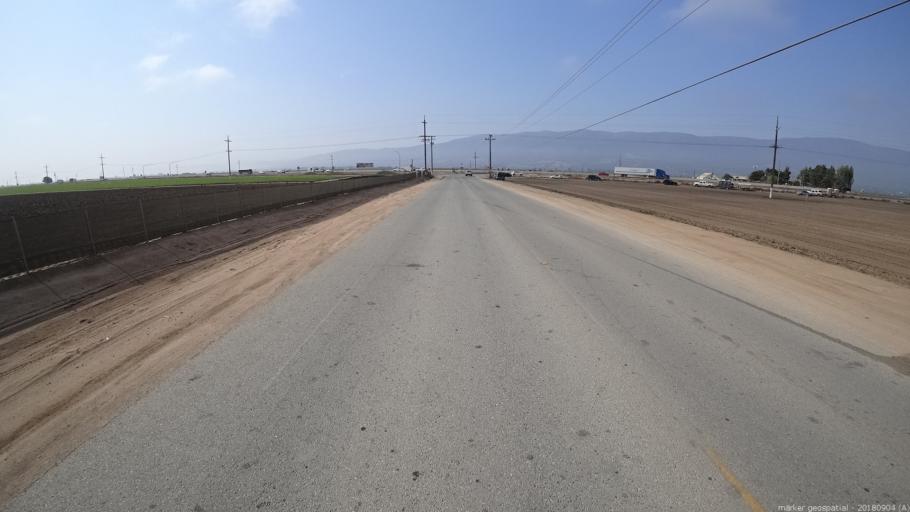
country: US
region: California
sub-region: Monterey County
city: Soledad
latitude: 36.4481
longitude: -121.3592
